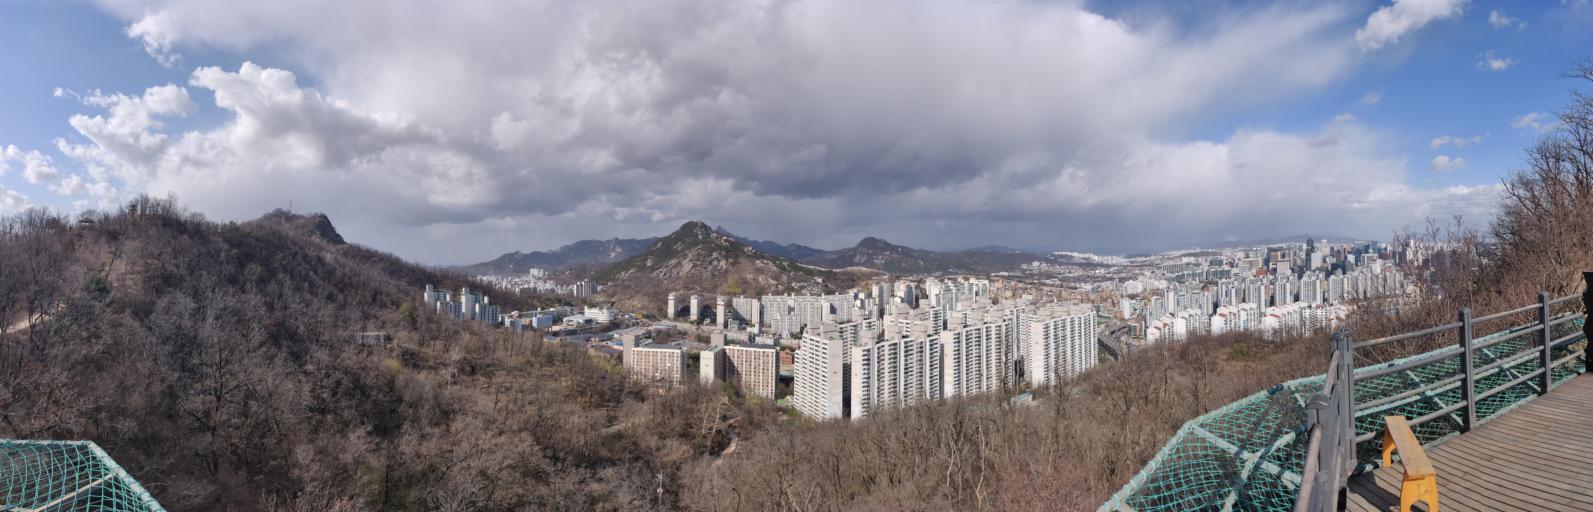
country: KR
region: Seoul
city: Seoul
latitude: 37.5698
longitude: 126.9538
